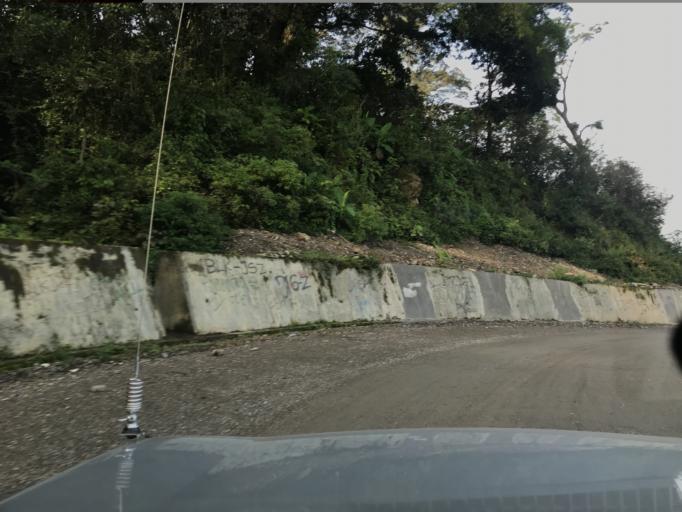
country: TL
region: Aileu
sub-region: Aileu Villa
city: Aileu
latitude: -8.6702
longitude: 125.5539
